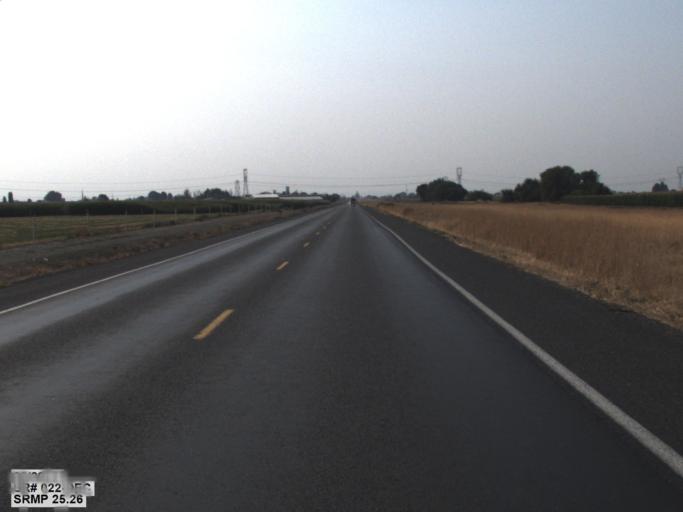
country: US
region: Washington
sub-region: Yakima County
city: Mabton
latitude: 46.2013
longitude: -119.9574
